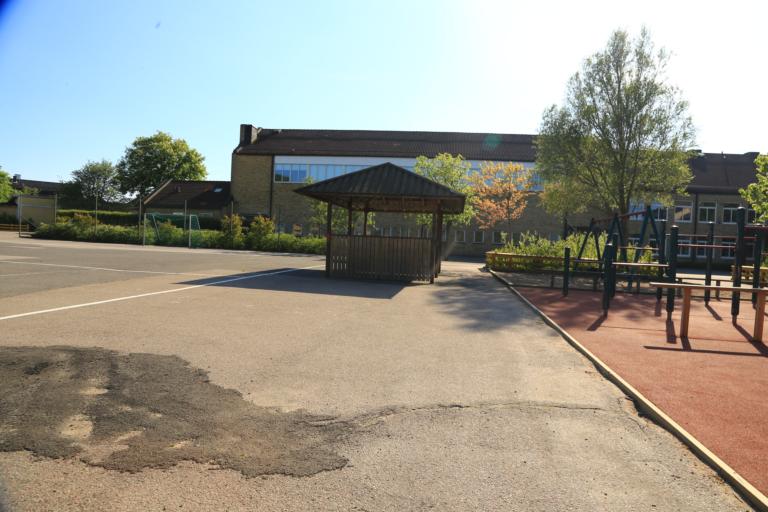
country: SE
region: Halland
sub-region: Varbergs Kommun
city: Varberg
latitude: 57.1103
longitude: 12.2602
